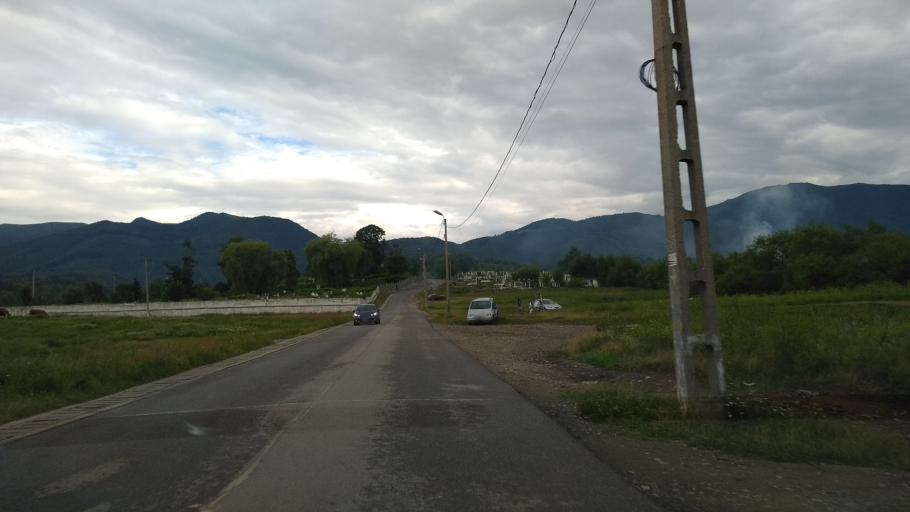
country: RO
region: Hunedoara
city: Vulcan
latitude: 45.3700
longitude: 23.2821
